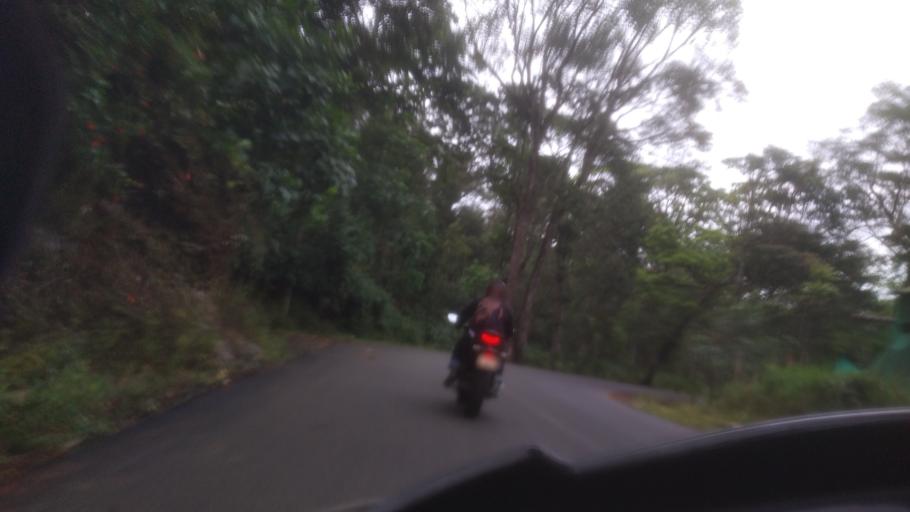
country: IN
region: Tamil Nadu
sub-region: Theni
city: Kombai
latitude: 9.8911
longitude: 77.1456
